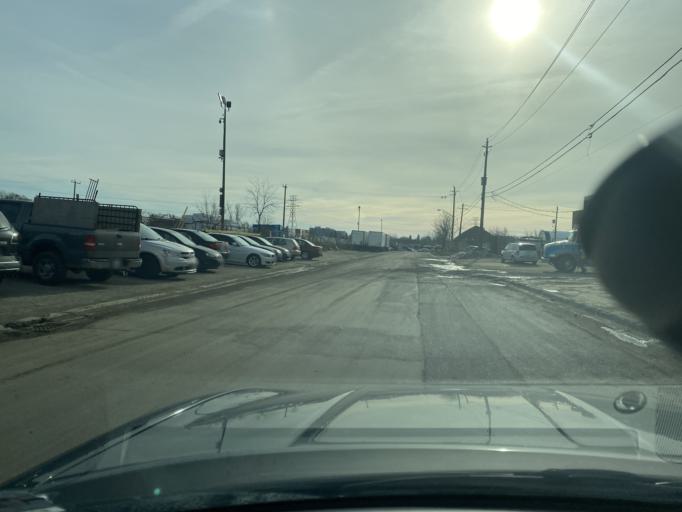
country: CA
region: Ontario
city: Scarborough
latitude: 43.7224
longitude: -79.2782
